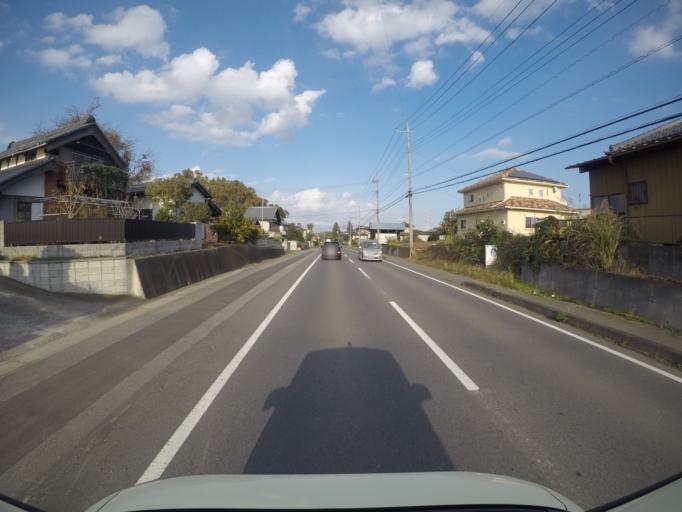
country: JP
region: Ibaraki
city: Ushiku
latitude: 36.0154
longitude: 140.0666
